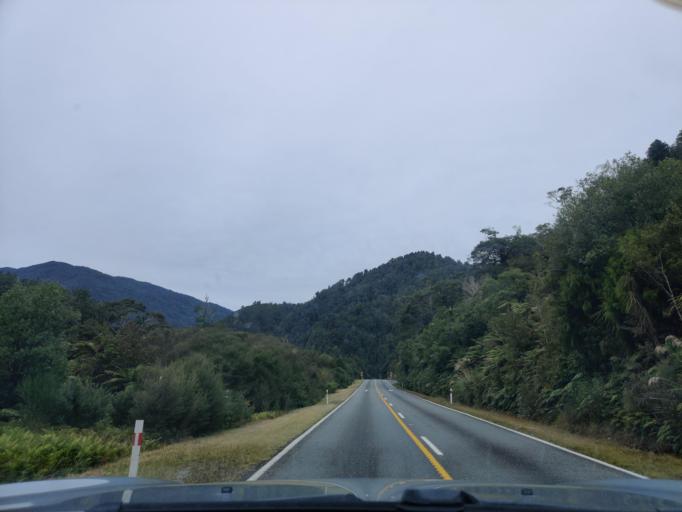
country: NZ
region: West Coast
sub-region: Buller District
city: Westport
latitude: -41.8481
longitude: 171.7258
